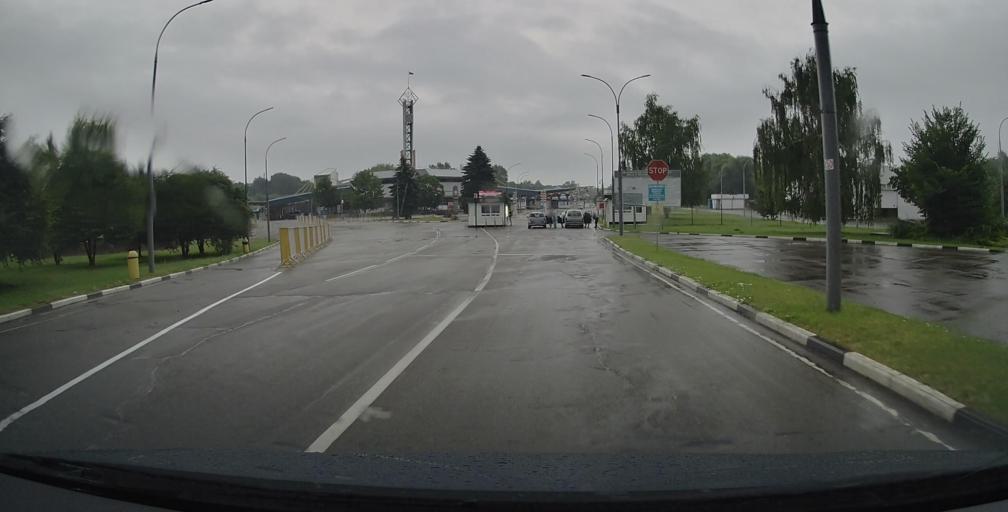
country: BY
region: Brest
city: Brest
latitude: 52.0729
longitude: 23.6564
